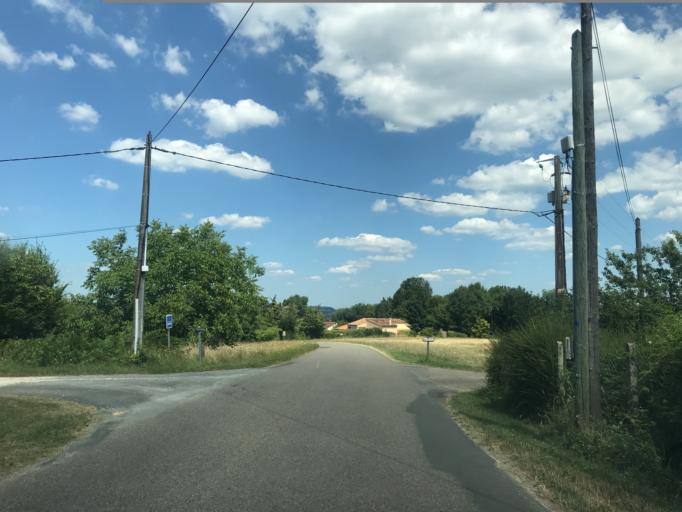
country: FR
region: Aquitaine
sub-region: Departement de la Dordogne
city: Sarlat-la-Caneda
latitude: 44.8472
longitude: 1.2029
